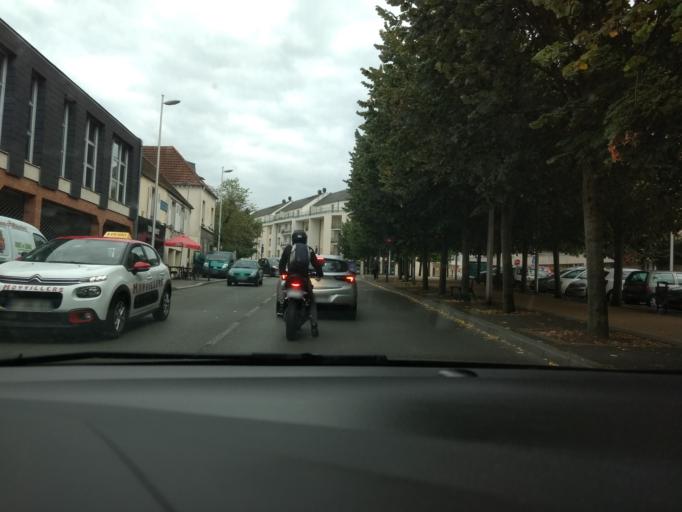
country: FR
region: Picardie
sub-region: Departement de l'Oise
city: Compiegne
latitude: 49.4154
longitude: 2.8198
